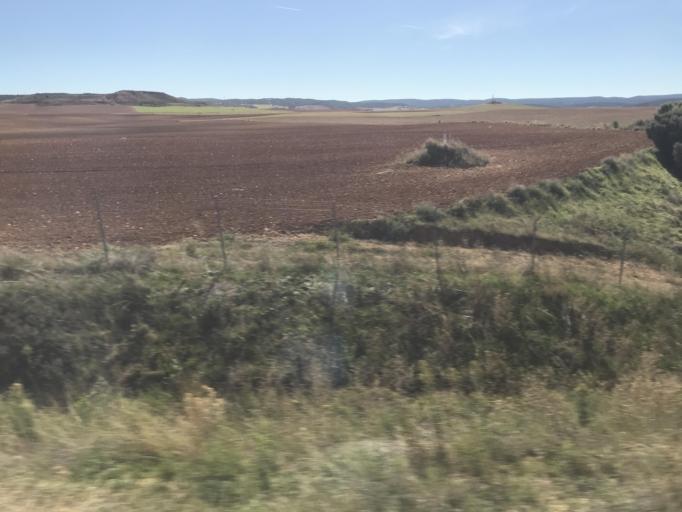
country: ES
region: Aragon
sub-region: Provincia de Zaragoza
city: Alconchel de Ariza
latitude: 41.2179
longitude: -2.1149
